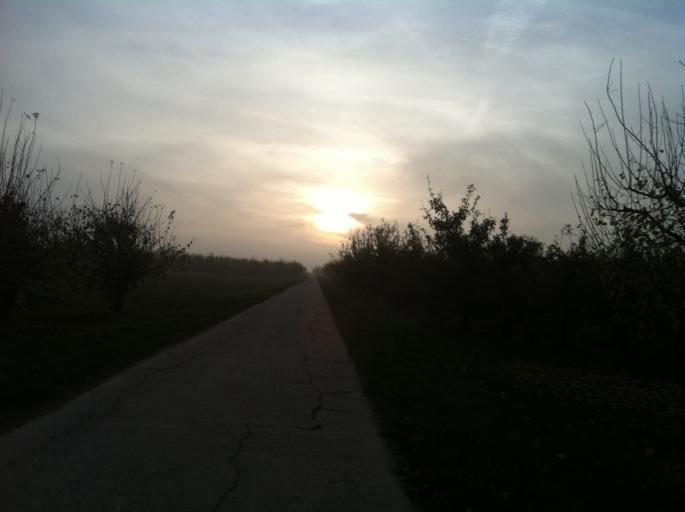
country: DE
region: Rheinland-Pfalz
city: Essenheim
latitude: 49.9611
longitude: 8.1473
